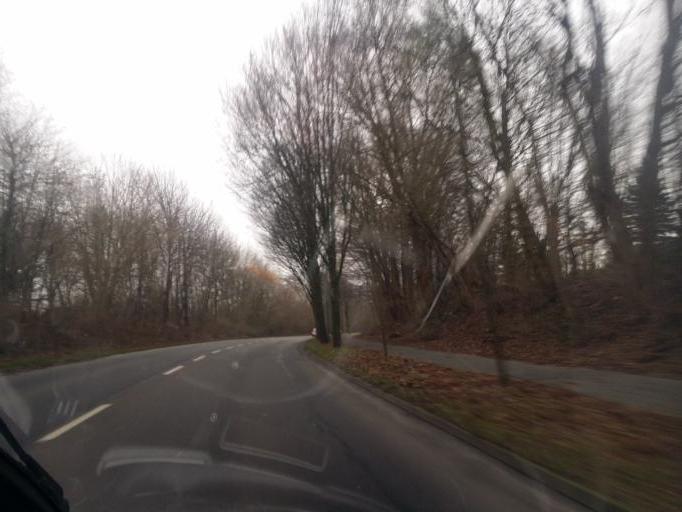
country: DE
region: Schleswig-Holstein
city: Heide
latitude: 54.2014
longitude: 9.1236
